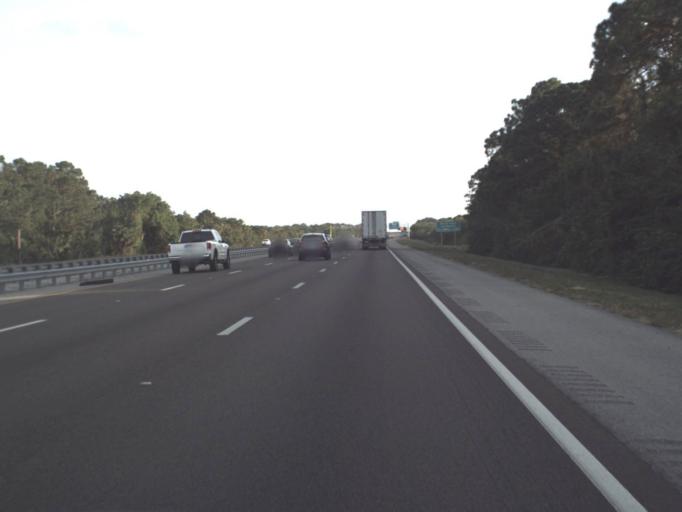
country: US
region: Florida
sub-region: Brevard County
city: Port Saint John
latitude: 28.4378
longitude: -80.8207
